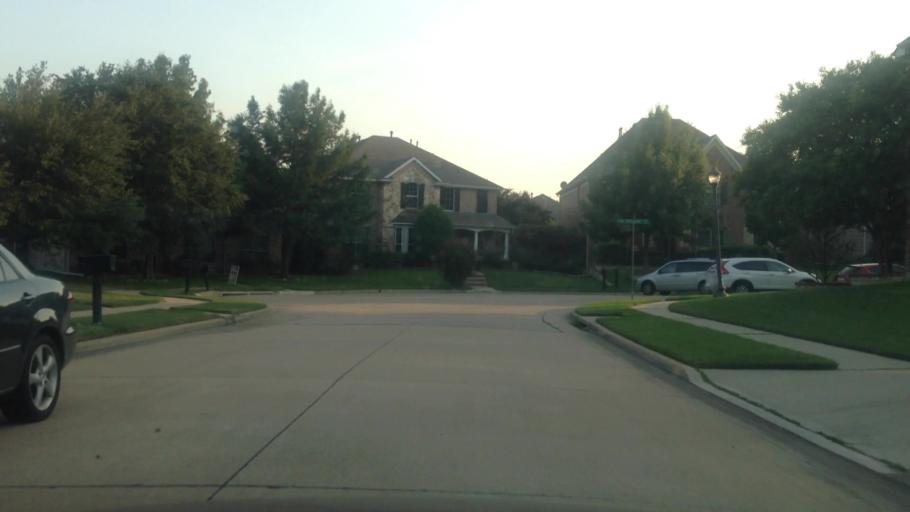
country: US
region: Texas
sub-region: Denton County
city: The Colony
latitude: 33.1254
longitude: -96.8707
